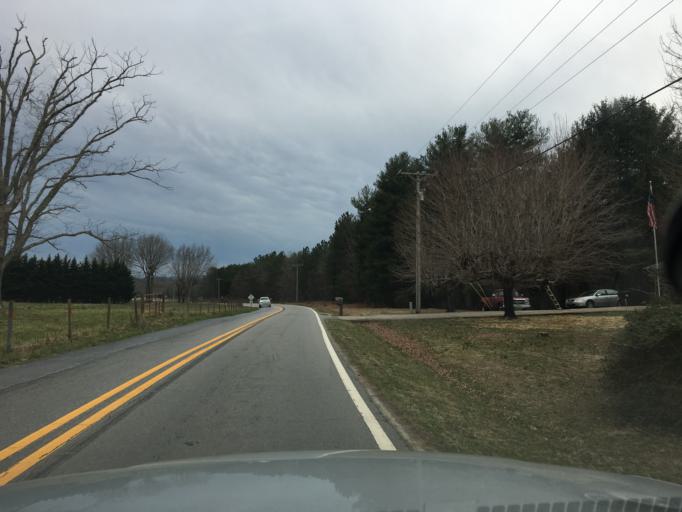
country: US
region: North Carolina
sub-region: Burke County
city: Glen Alpine
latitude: 35.6951
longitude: -81.8399
